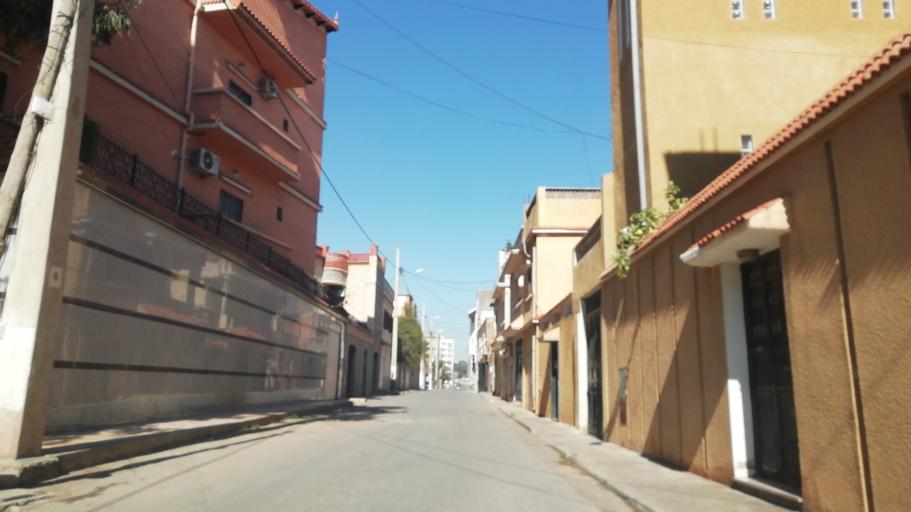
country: DZ
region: Oran
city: Oran
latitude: 35.6737
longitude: -0.6329
